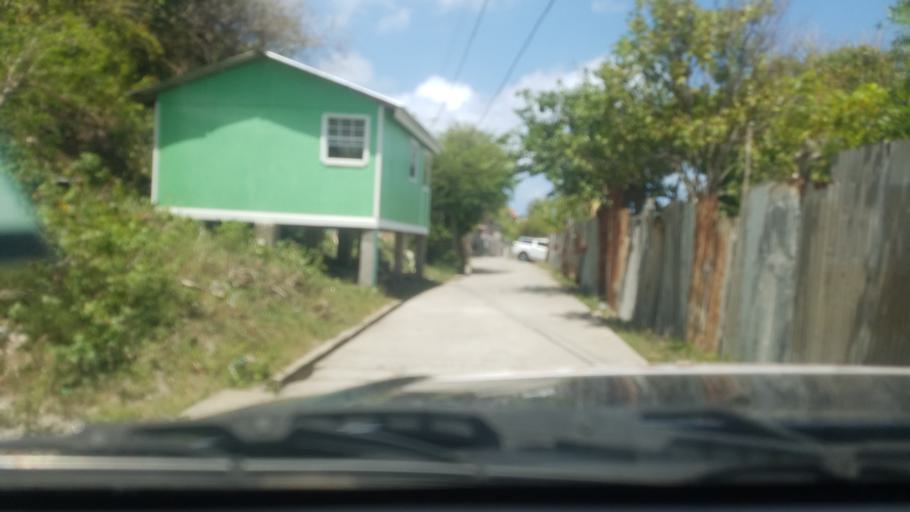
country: LC
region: Vieux-Fort
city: Vieux Fort
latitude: 13.7247
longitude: -60.9497
